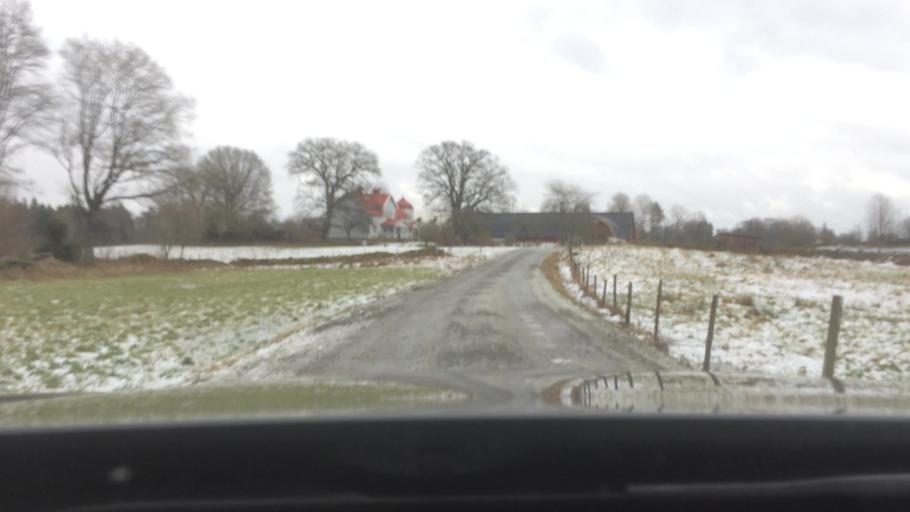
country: SE
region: Vaestra Goetaland
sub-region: Falkopings Kommun
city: Floby
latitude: 57.9991
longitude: 13.3856
